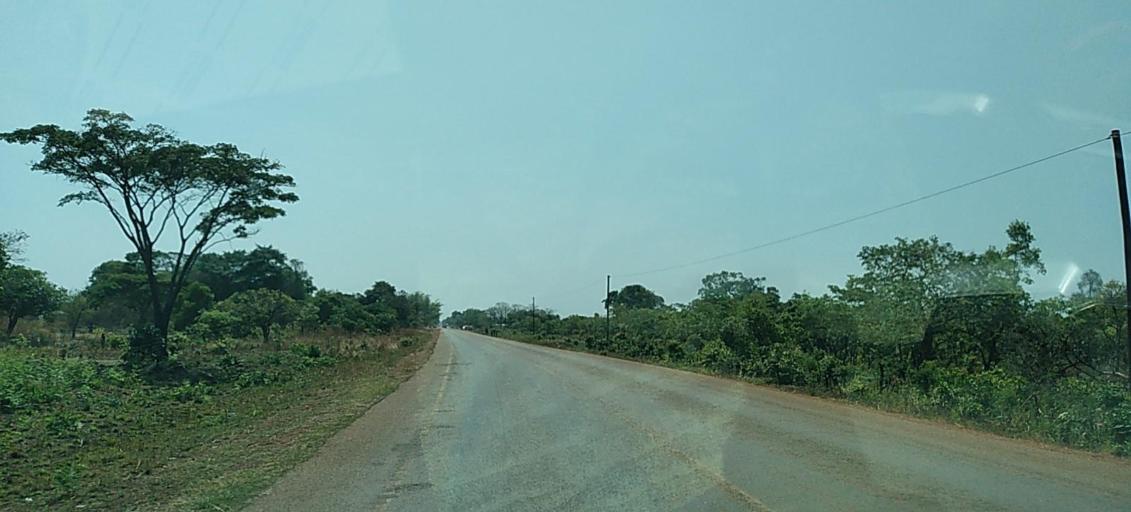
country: ZM
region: North-Western
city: Solwezi
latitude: -12.3612
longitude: 25.9367
